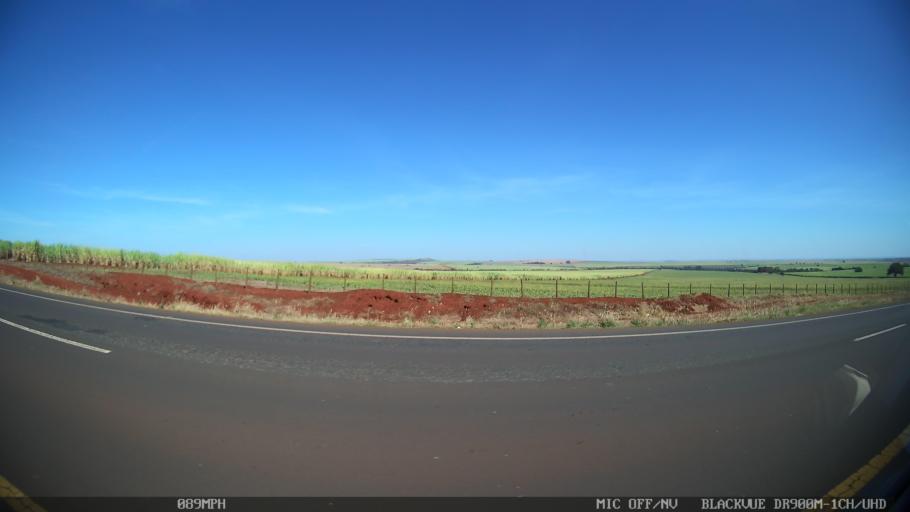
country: BR
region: Sao Paulo
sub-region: Ipua
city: Ipua
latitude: -20.4710
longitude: -48.1090
